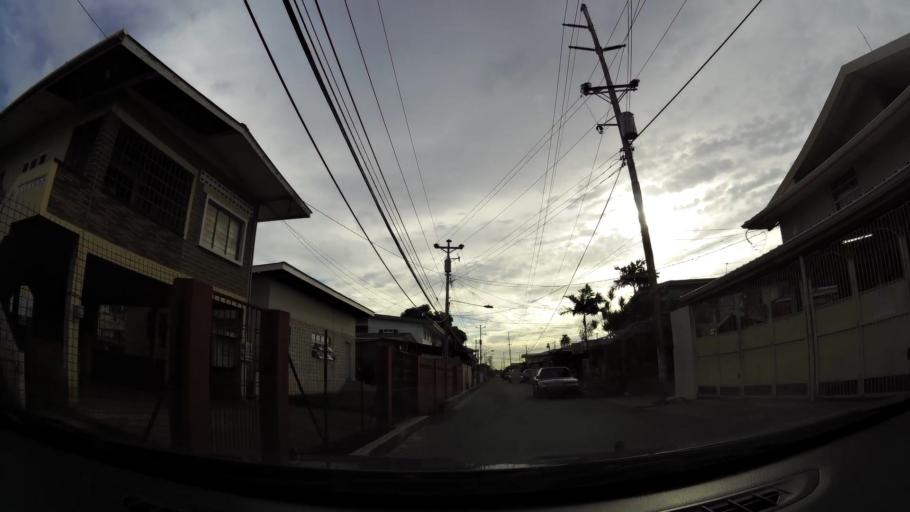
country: TT
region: Tunapuna/Piarco
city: Tunapuna
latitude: 10.6391
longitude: -61.4103
